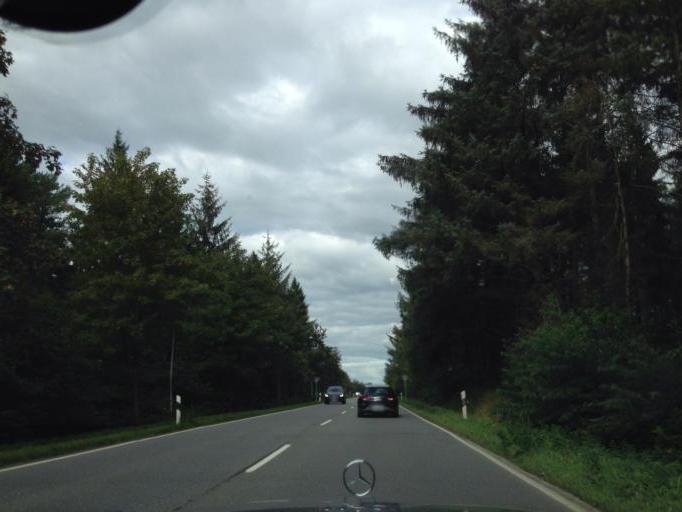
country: DE
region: Schleswig-Holstein
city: Leck
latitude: 54.7524
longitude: 8.9683
